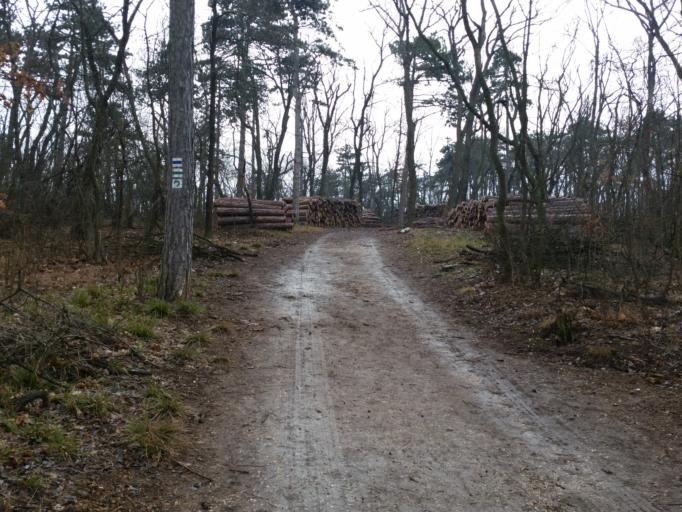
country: HU
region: Budapest
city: Budapest II. keruelet
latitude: 47.5369
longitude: 18.9997
